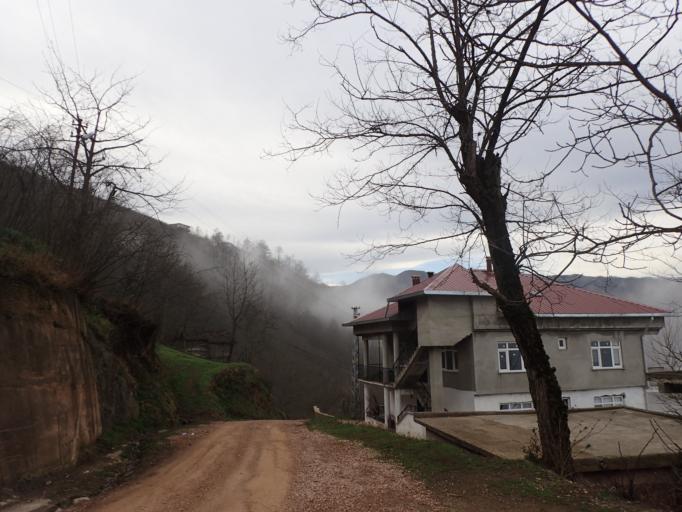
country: TR
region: Ordu
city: Camas
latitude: 40.8908
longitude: 37.5144
